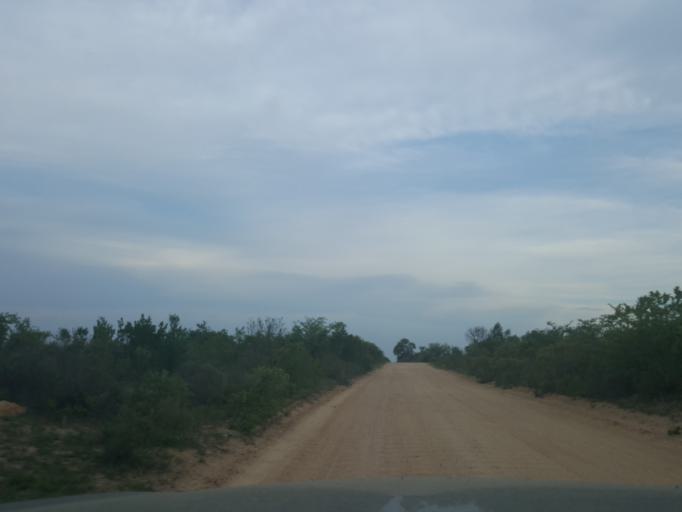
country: ZA
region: Limpopo
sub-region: Mopani District Municipality
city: Hoedspruit
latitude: -24.5856
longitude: 30.9755
